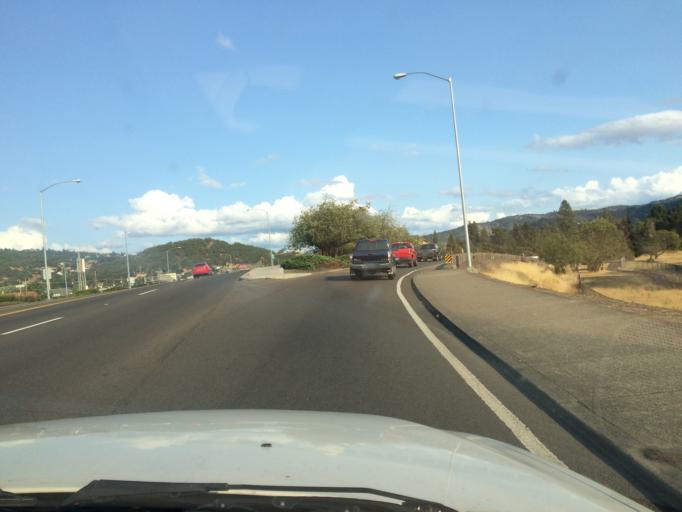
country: US
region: Oregon
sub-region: Douglas County
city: Roseburg
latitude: 43.2273
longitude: -123.3630
